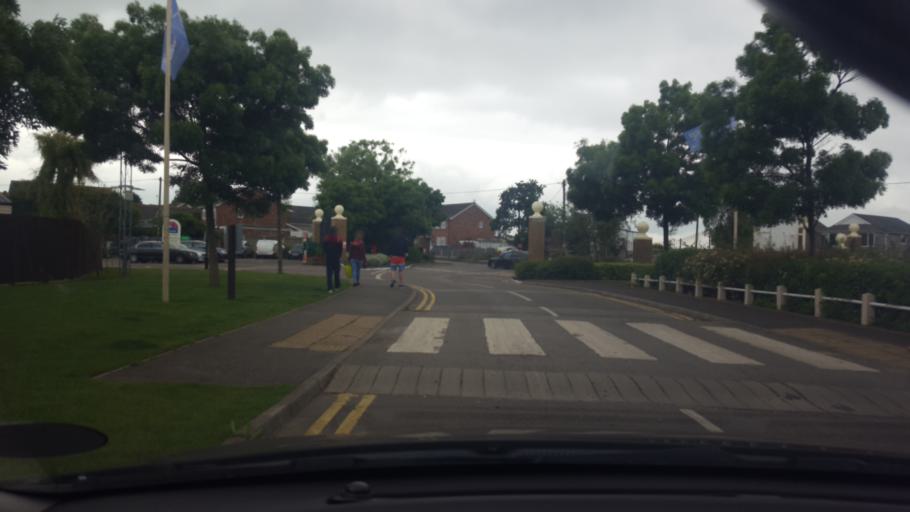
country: GB
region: England
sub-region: Essex
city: Brightlingsea
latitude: 51.7960
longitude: 1.0320
